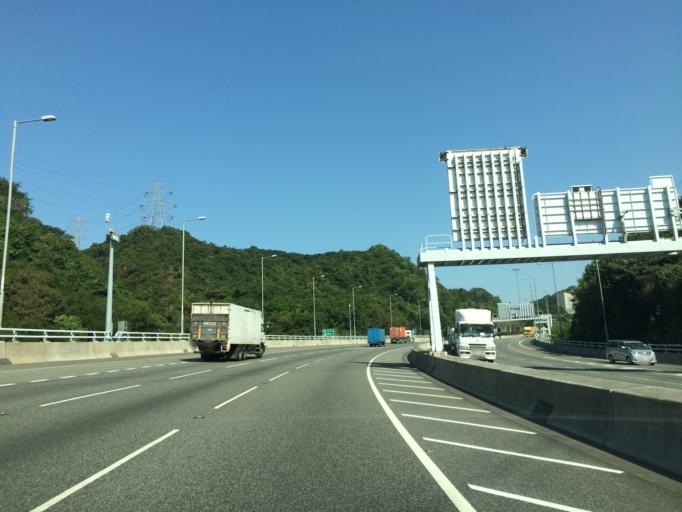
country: HK
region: Sham Shui Po
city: Sham Shui Po
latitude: 22.3423
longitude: 114.1435
